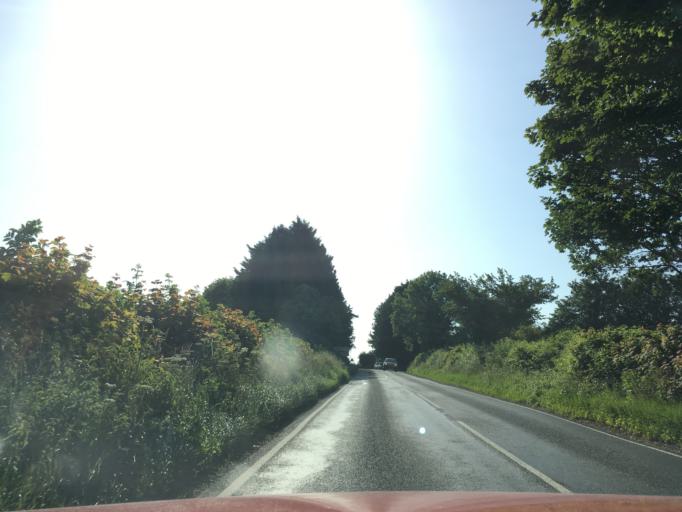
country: GB
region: England
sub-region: Oxfordshire
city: Somerton
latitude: 51.9222
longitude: -1.3211
